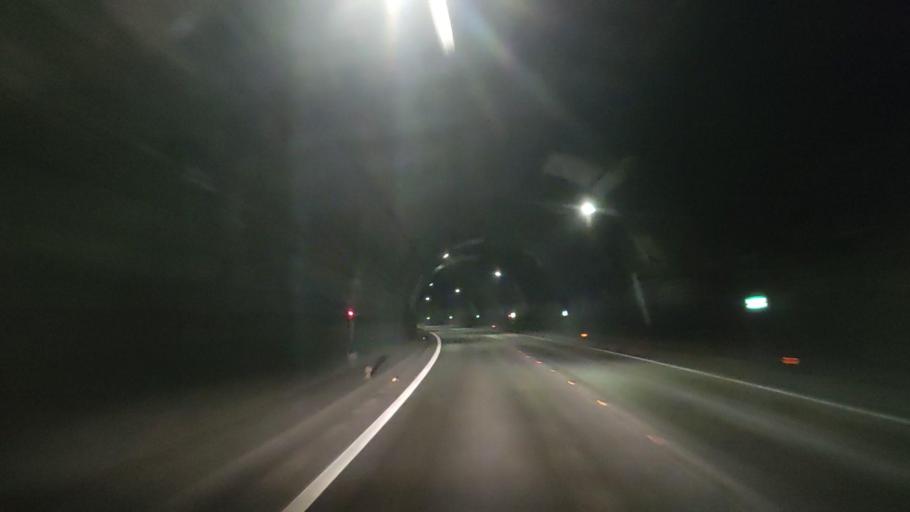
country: JP
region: Gifu
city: Gifu-shi
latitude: 35.4359
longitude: 136.7772
